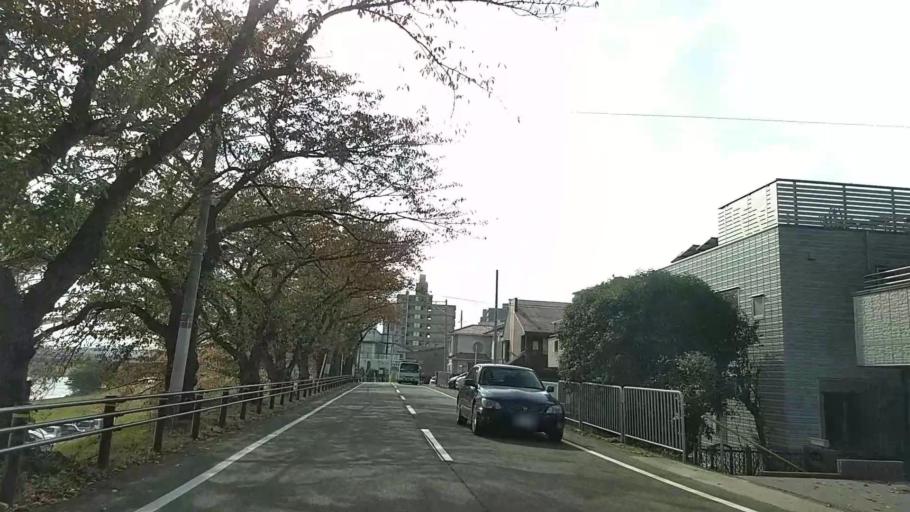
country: JP
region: Kanagawa
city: Atsugi
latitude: 35.4476
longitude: 139.3686
